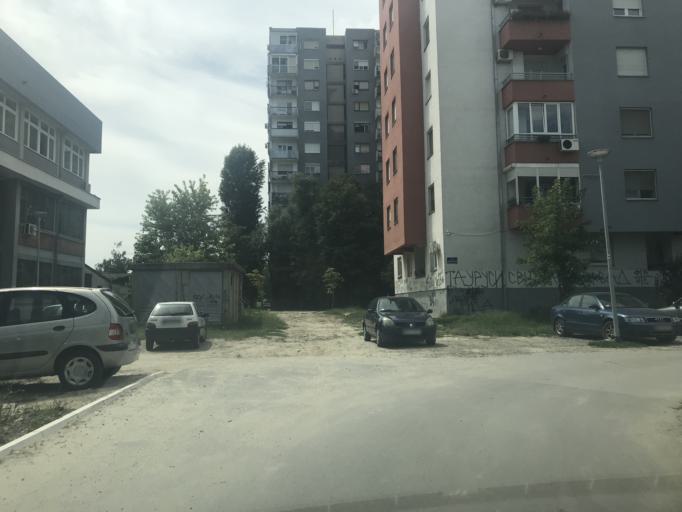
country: RS
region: Autonomna Pokrajina Vojvodina
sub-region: Juznobacki Okrug
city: Novi Sad
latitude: 45.2637
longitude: 19.8083
